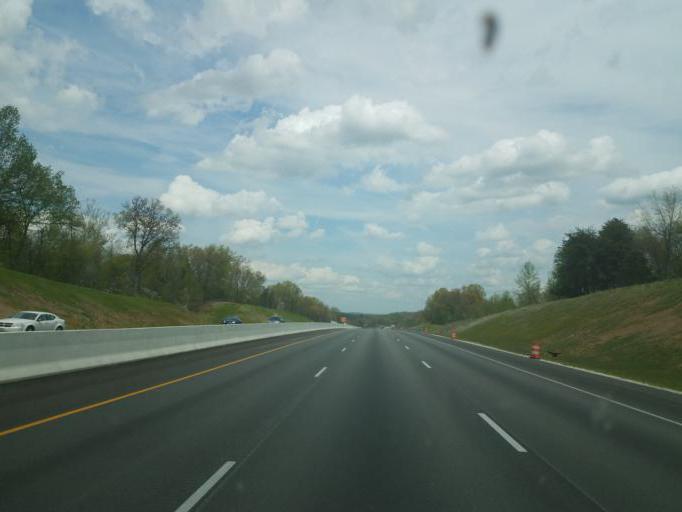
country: US
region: Kentucky
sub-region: Hart County
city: Munfordville
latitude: 37.3244
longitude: -85.9062
